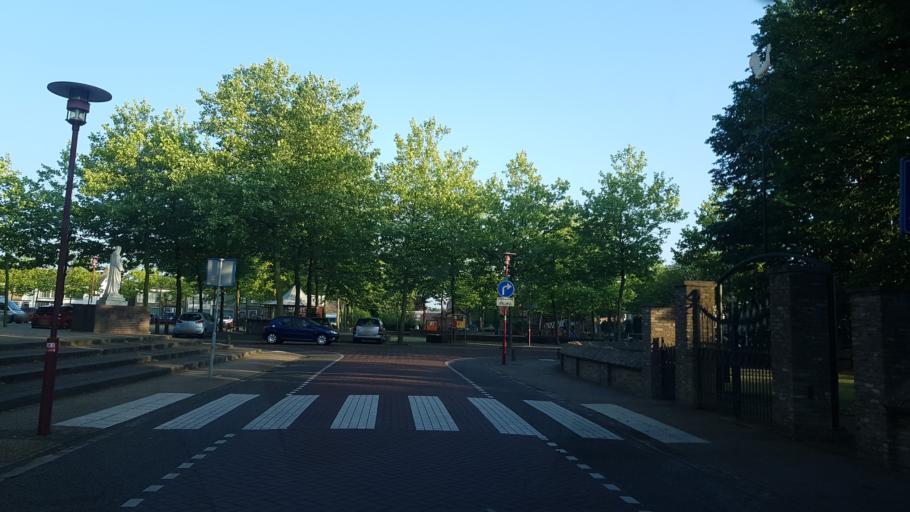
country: NL
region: North Brabant
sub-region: Gemeente Breda
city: Hoge Vucht
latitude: 51.6115
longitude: 4.8174
